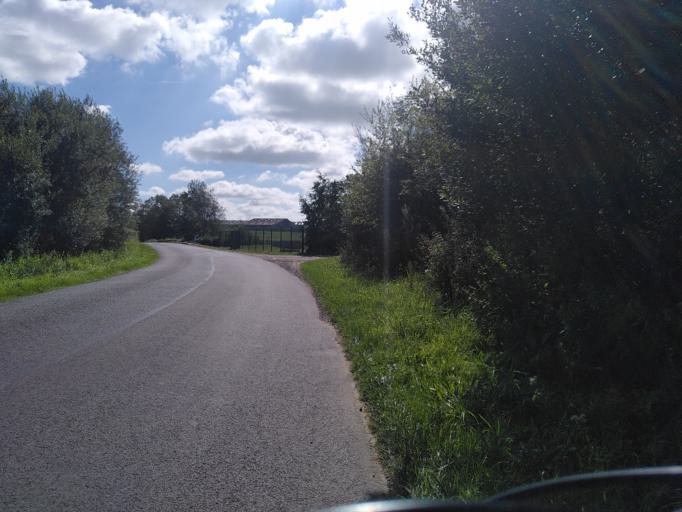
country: FR
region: Nord-Pas-de-Calais
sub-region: Departement du Pas-de-Calais
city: Ambleteuse
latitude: 50.7981
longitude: 1.6309
